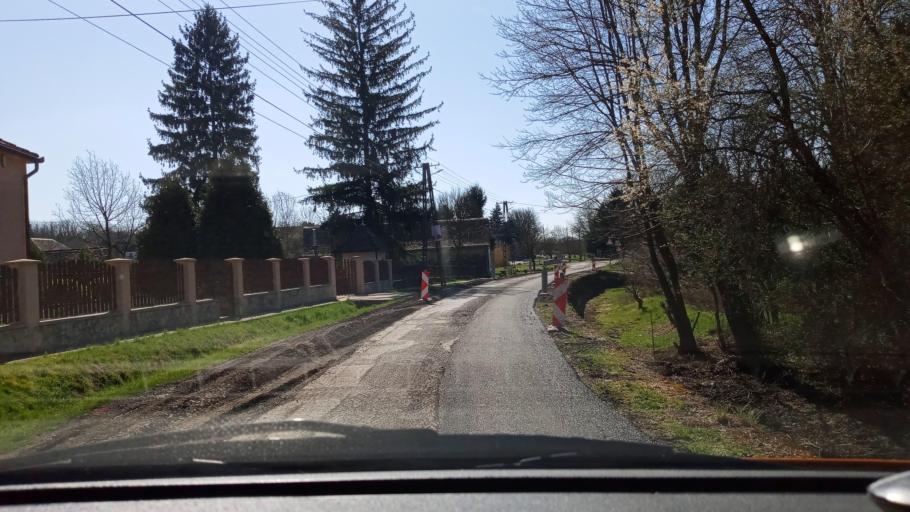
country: HU
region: Baranya
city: Kozarmisleny
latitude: 46.0196
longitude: 18.4076
